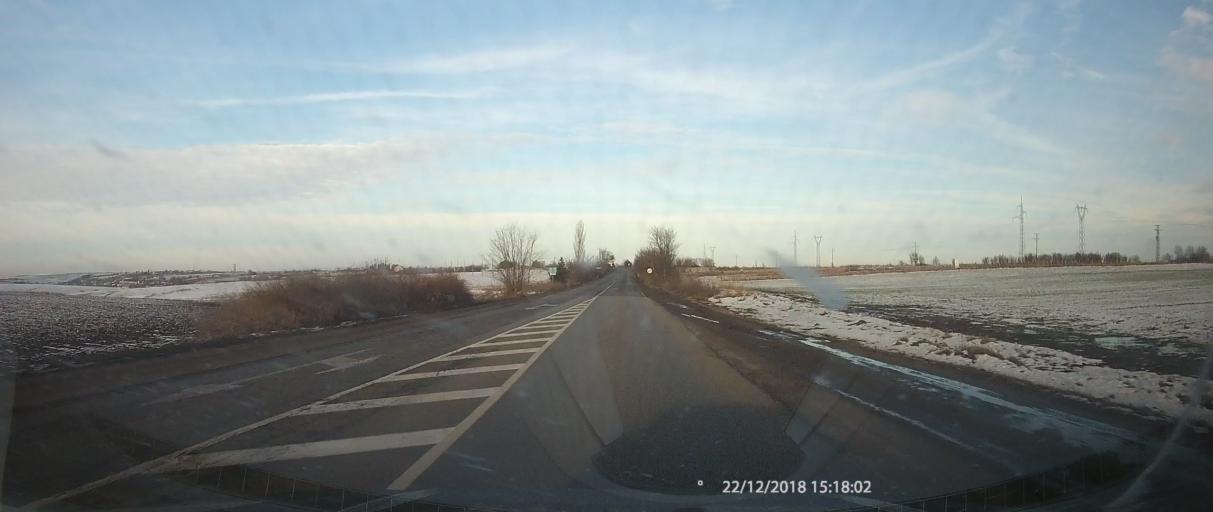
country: BG
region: Ruse
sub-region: Obshtina Dve Mogili
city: Dve Mogili
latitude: 43.6339
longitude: 25.8677
